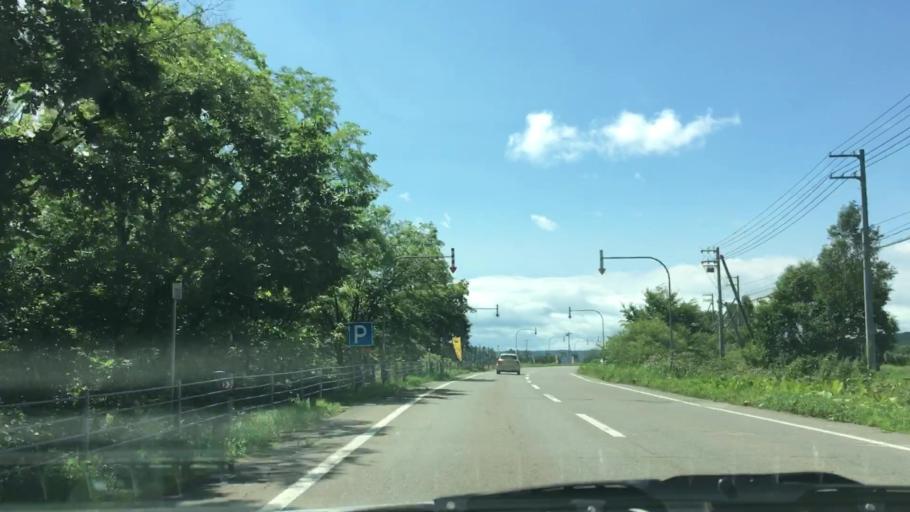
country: JP
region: Hokkaido
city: Otofuke
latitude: 43.2809
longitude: 143.6248
